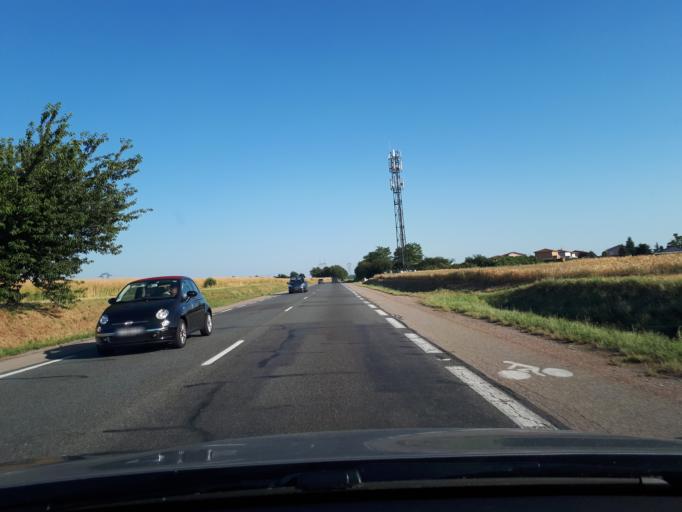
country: FR
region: Rhone-Alpes
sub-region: Departement du Rhone
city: Genas
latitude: 45.7361
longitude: 5.0256
